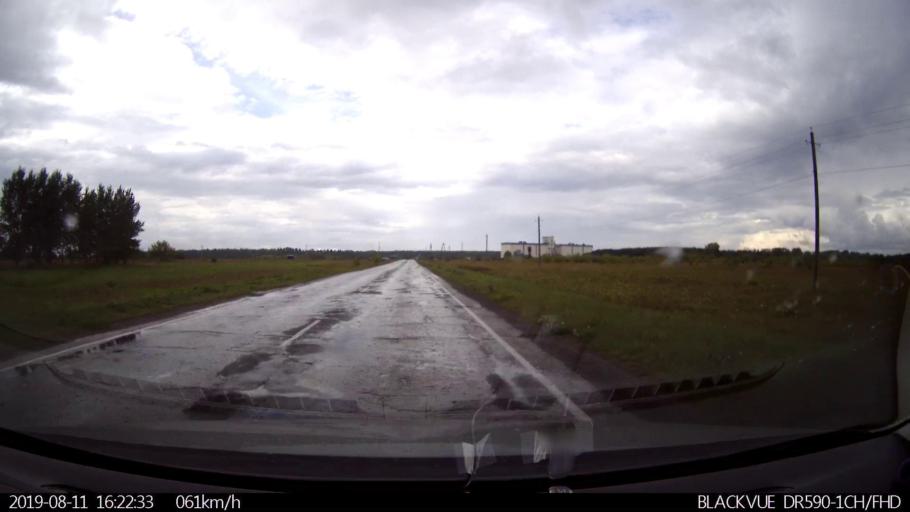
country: RU
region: Ulyanovsk
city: Mayna
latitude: 54.0889
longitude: 47.5924
